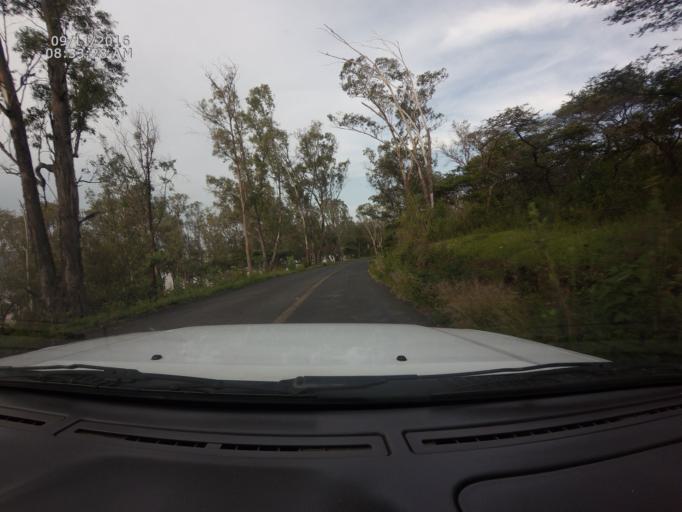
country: MX
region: Michoacan
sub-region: Morelia
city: Morelos
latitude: 19.6285
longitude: -101.2539
